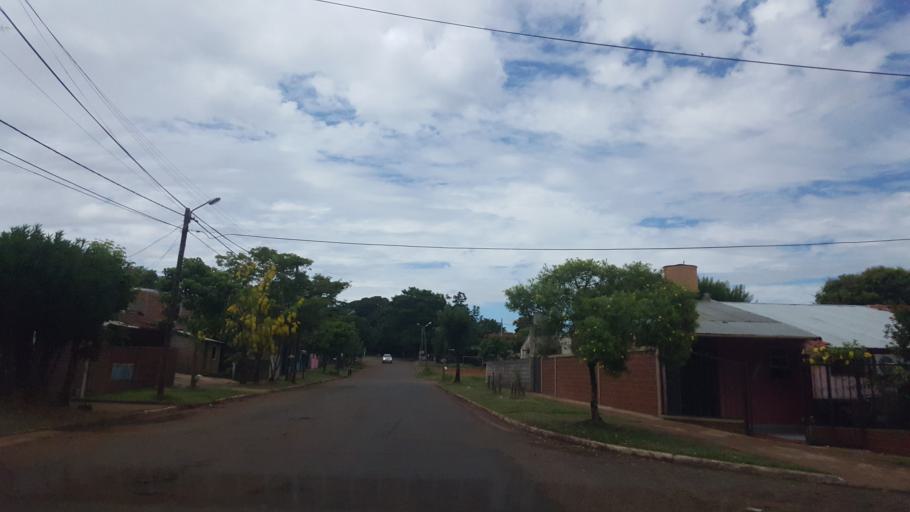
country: AR
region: Misiones
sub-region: Departamento de Capital
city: Posadas
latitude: -27.4247
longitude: -55.8865
